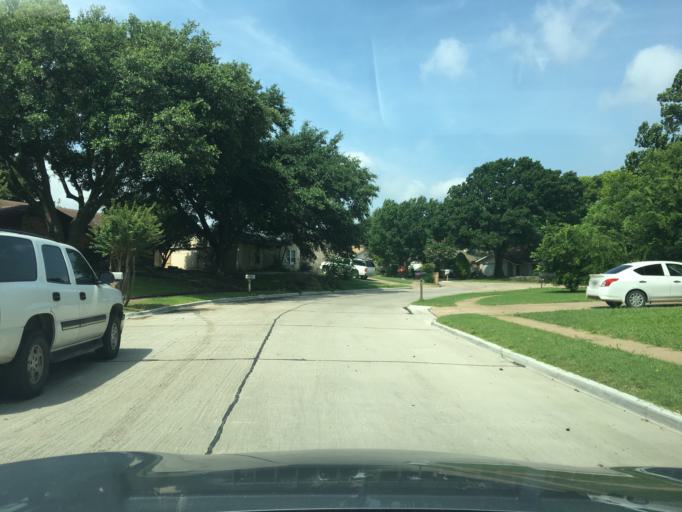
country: US
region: Texas
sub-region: Dallas County
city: Garland
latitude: 32.9299
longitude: -96.6721
